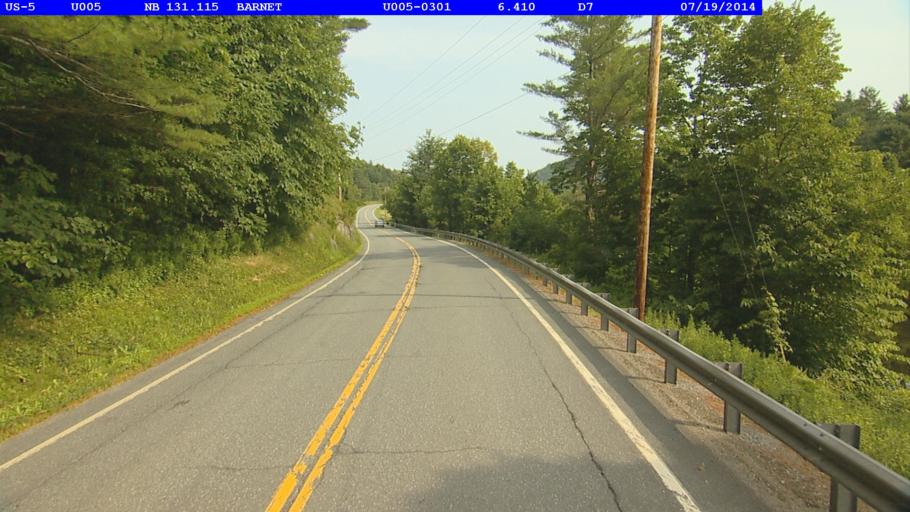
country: US
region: Vermont
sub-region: Caledonia County
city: Saint Johnsbury
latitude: 44.3365
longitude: -72.0424
